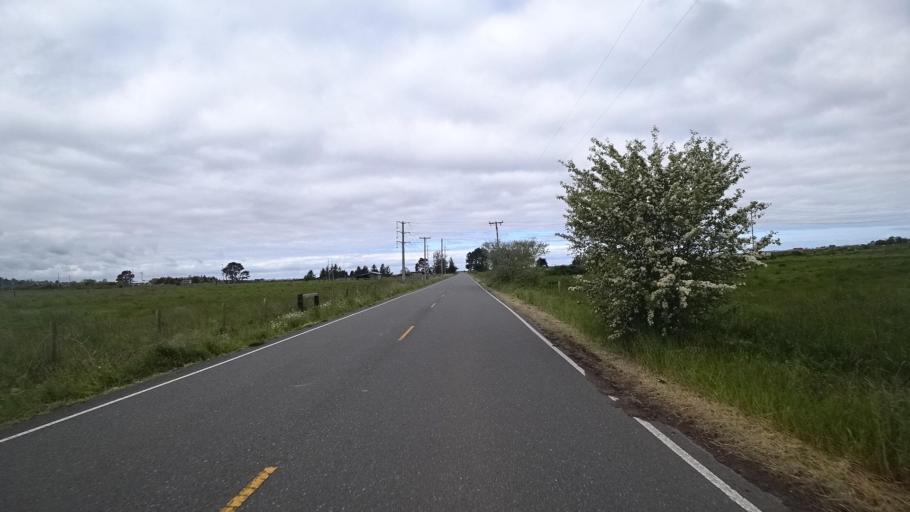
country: US
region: California
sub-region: Humboldt County
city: Bayside
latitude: 40.8350
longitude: -124.0763
